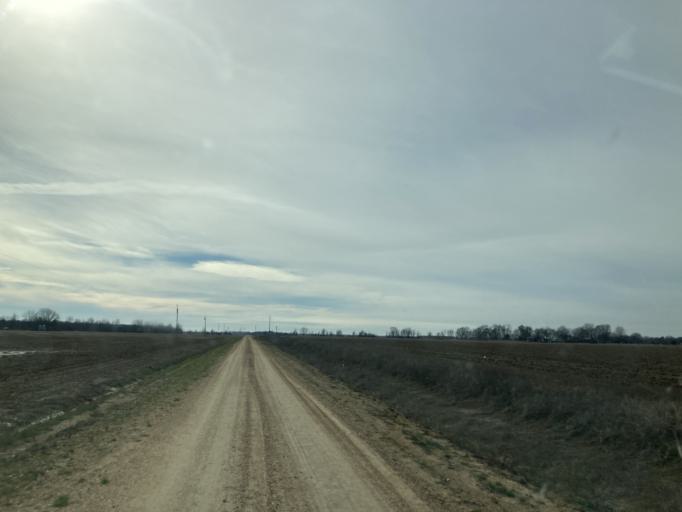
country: US
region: Mississippi
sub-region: Humphreys County
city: Belzoni
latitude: 33.0659
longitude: -90.6577
